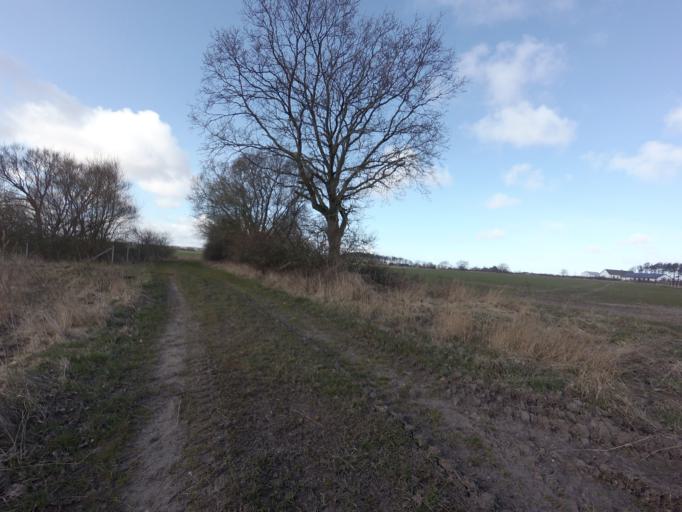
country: SE
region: Skane
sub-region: Helsingborg
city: Odakra
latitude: 56.1546
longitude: 12.7045
